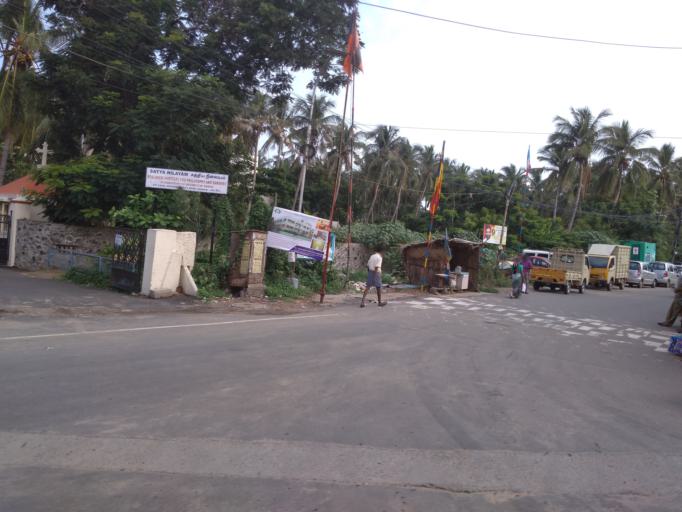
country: IN
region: Tamil Nadu
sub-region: Chennai
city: Gandhi Nagar
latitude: 12.9822
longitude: 80.2545
